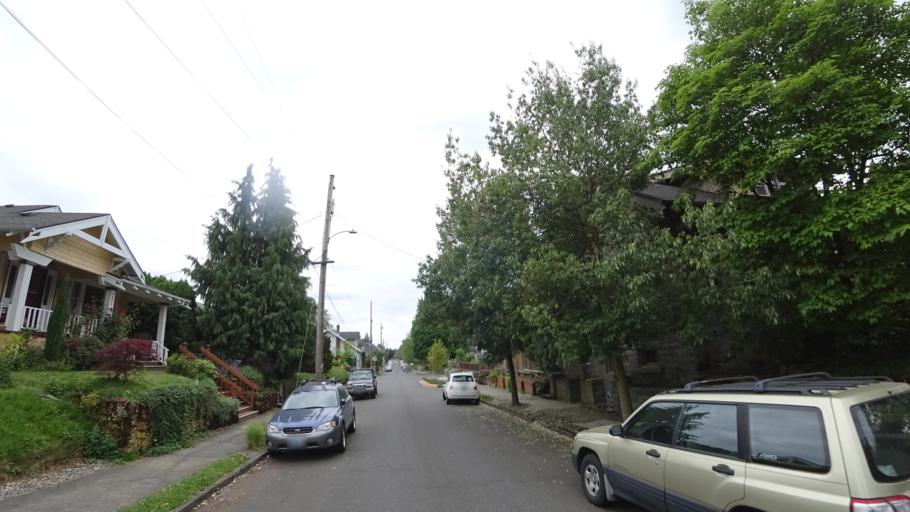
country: US
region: Oregon
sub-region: Multnomah County
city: Lents
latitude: 45.5141
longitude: -122.6151
